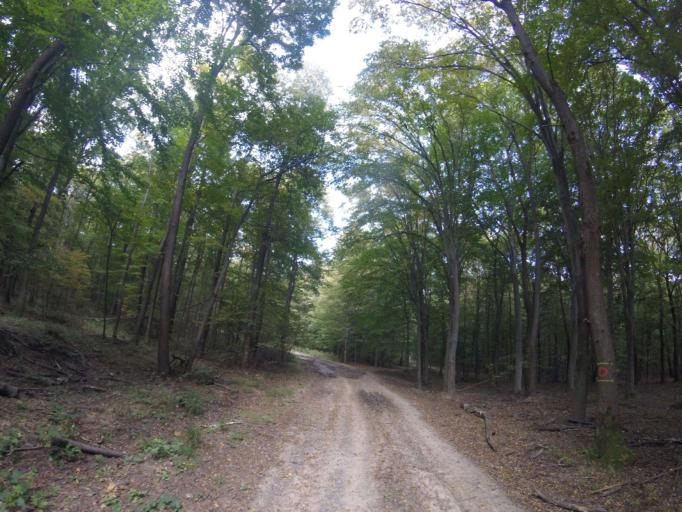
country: HU
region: Komarom-Esztergom
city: Kesztolc
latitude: 47.7681
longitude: 18.8169
